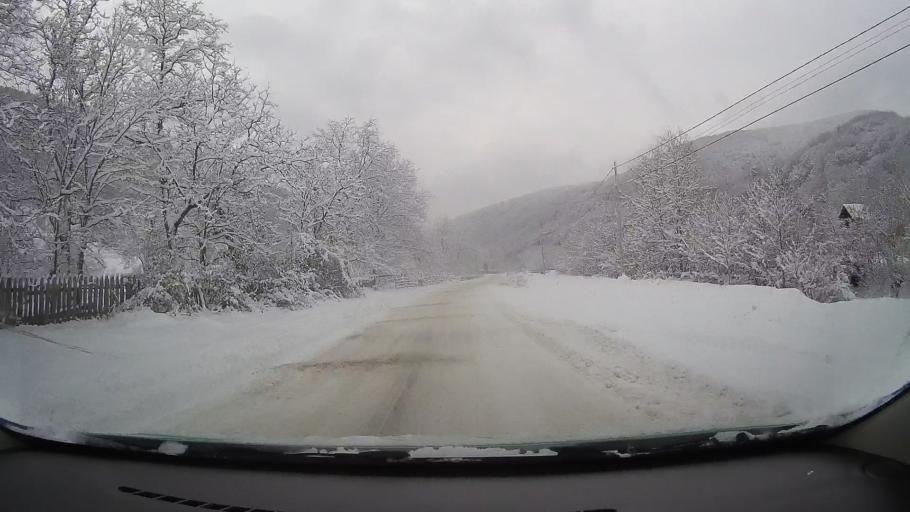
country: RO
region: Alba
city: Pianu de Sus
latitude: 45.8813
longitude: 23.4920
